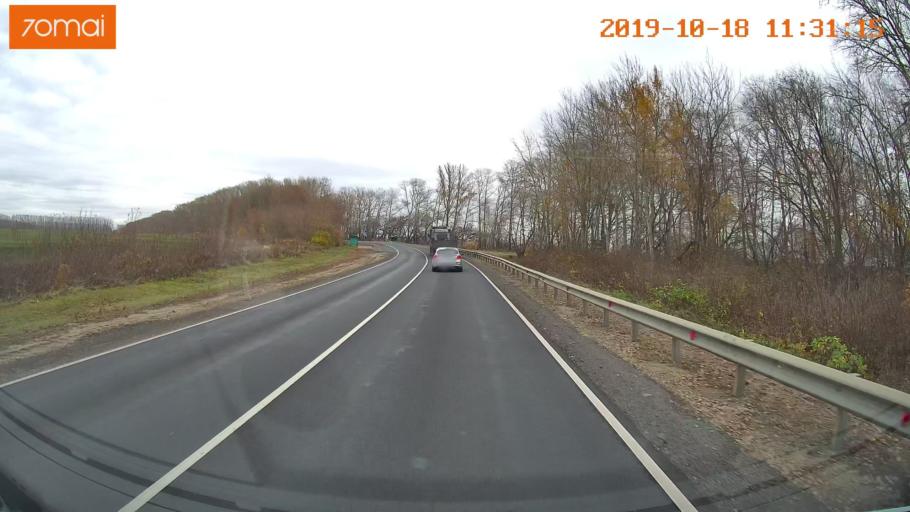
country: RU
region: Rjazan
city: Oktyabr'skiy
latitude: 54.1416
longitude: 38.6928
